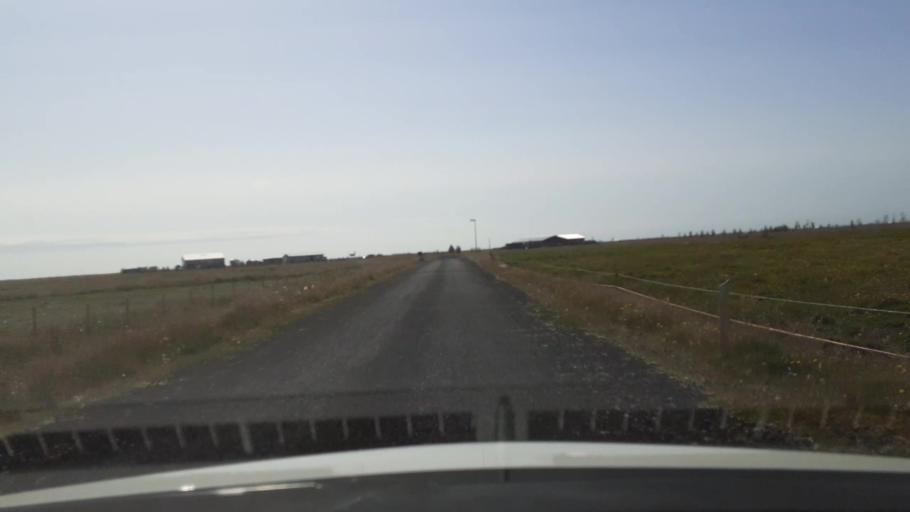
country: IS
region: South
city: Selfoss
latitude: 63.8881
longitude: -21.0904
